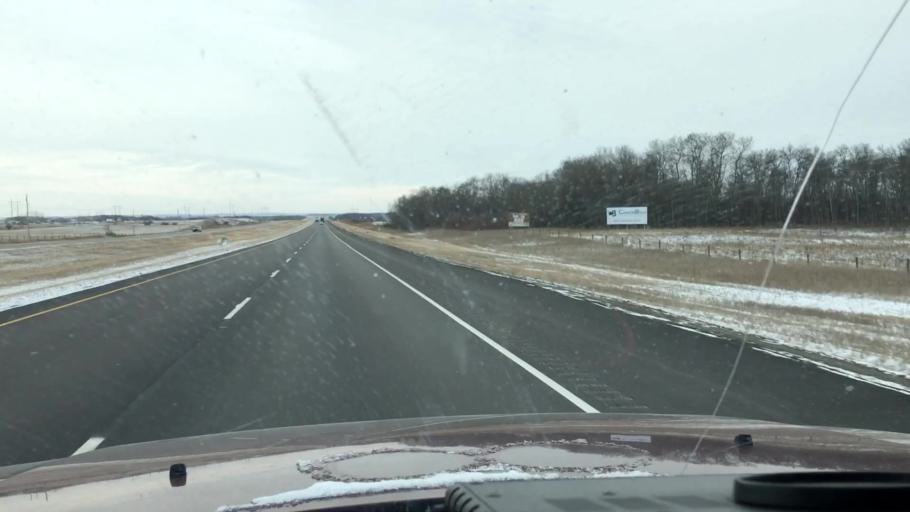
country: CA
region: Saskatchewan
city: Saskatoon
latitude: 51.9017
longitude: -106.5221
